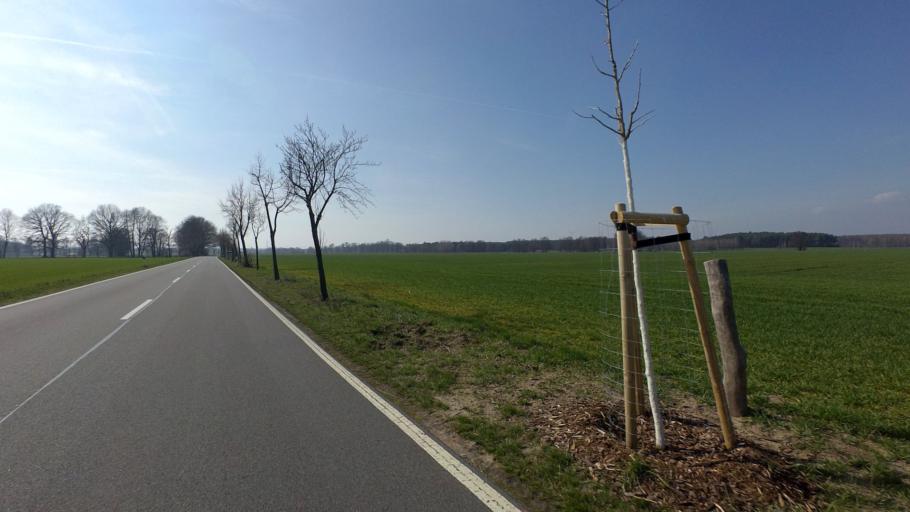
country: DE
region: Brandenburg
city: Drahnsdorf
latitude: 51.9269
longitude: 13.5945
